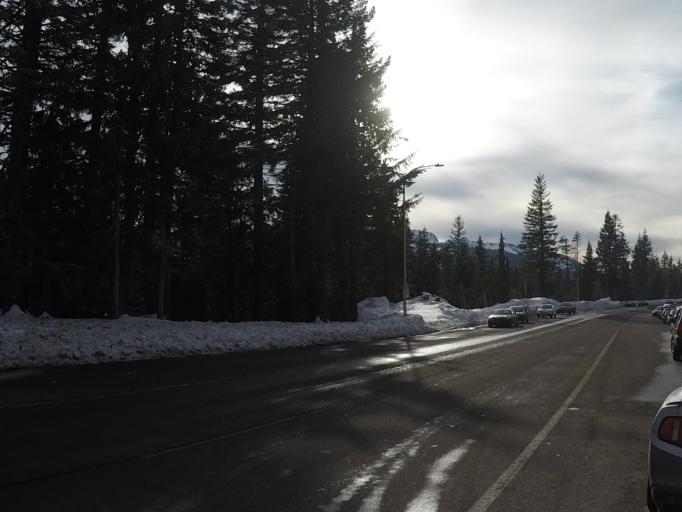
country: US
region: Oregon
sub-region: Clackamas County
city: Mount Hood Village
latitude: 45.3004
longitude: -121.7437
